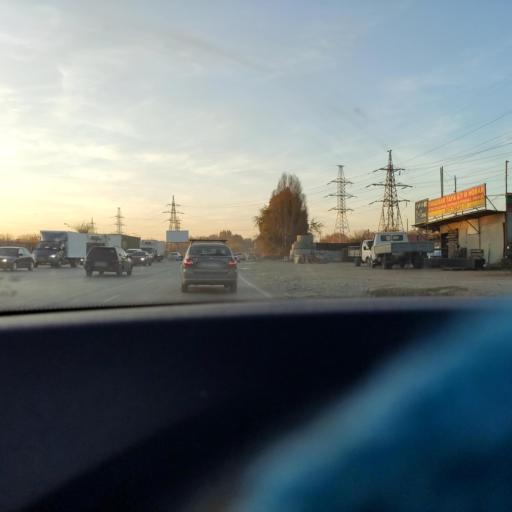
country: RU
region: Samara
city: Petra-Dubrava
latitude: 53.2582
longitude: 50.2941
